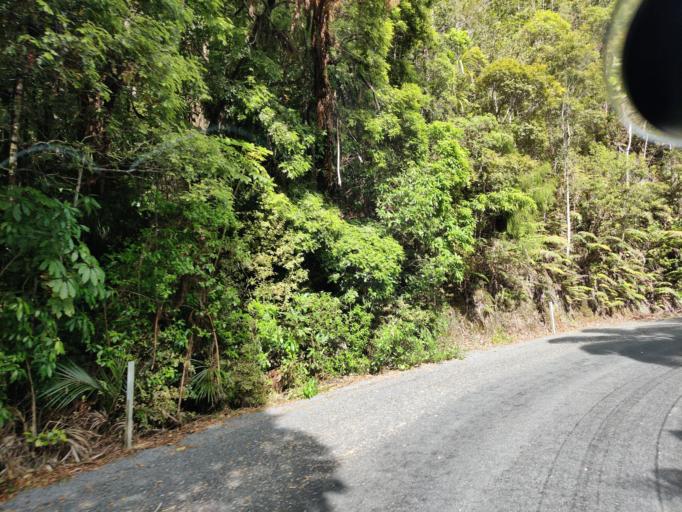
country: NZ
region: Northland
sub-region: Kaipara District
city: Dargaville
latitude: -35.6497
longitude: 173.5653
